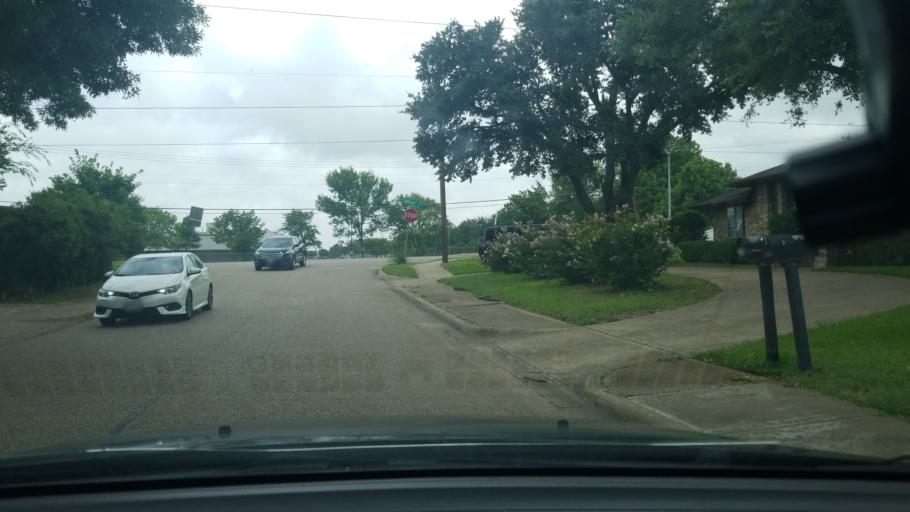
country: US
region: Texas
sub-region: Dallas County
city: Balch Springs
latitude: 32.7920
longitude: -96.6883
